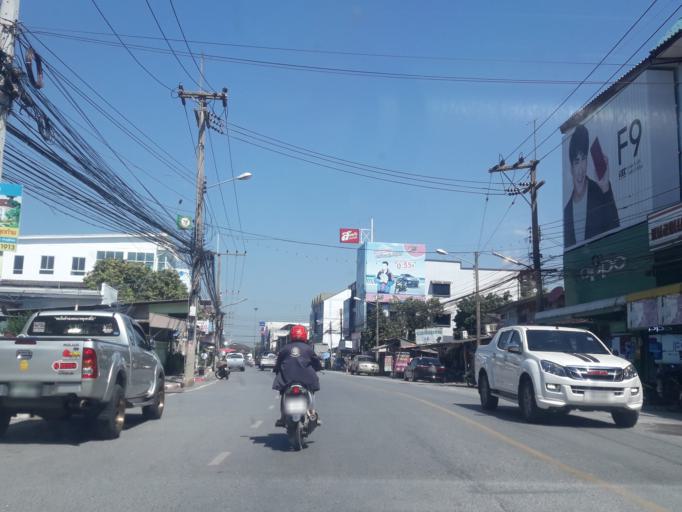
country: TH
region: Sara Buri
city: Nong Khae
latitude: 14.3440
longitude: 100.8671
